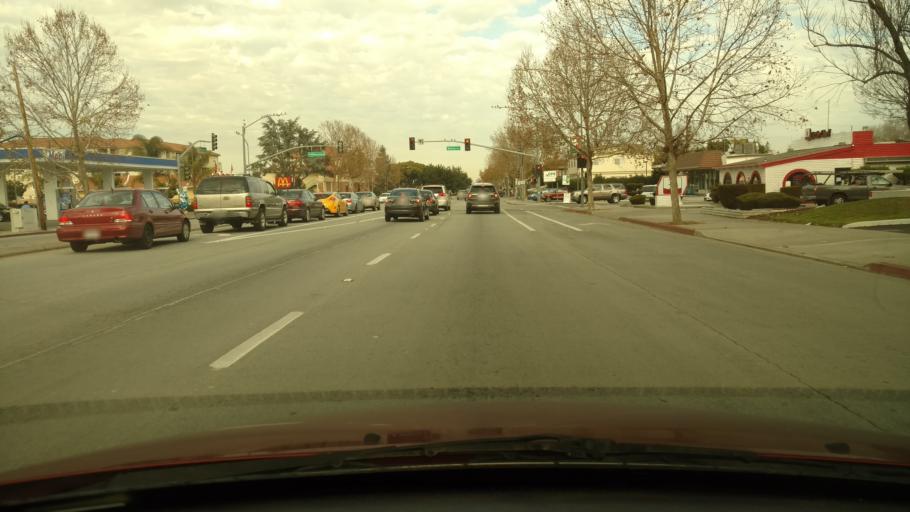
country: US
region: California
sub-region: Santa Clara County
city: Campbell
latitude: 37.2970
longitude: -121.9499
